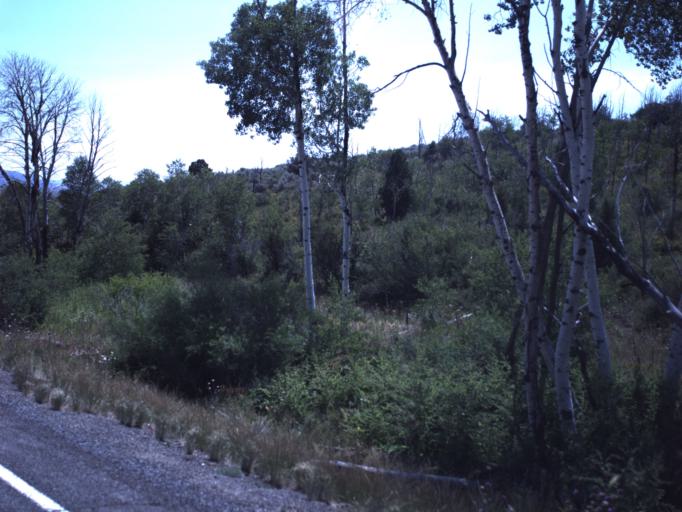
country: US
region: Utah
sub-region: Carbon County
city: Helper
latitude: 39.8582
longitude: -111.0523
